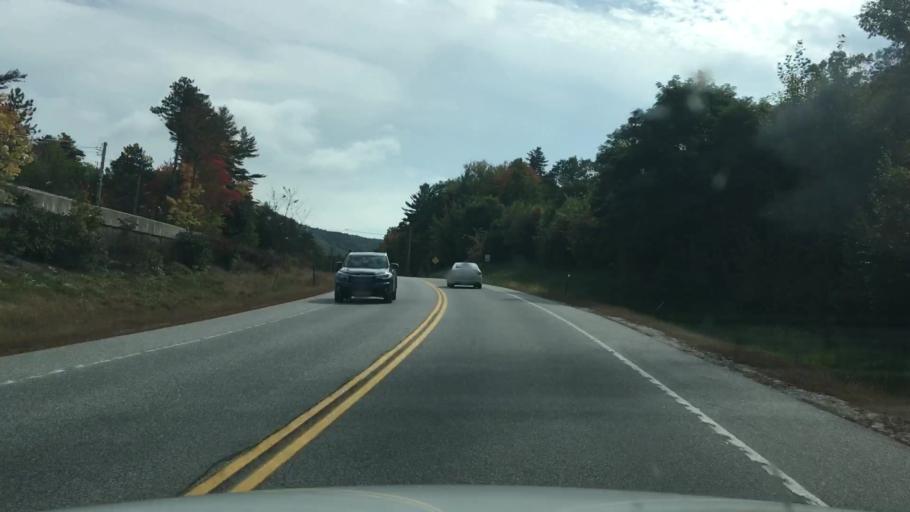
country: US
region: New Hampshire
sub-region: Carroll County
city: North Conway
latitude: 44.0439
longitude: -71.1216
